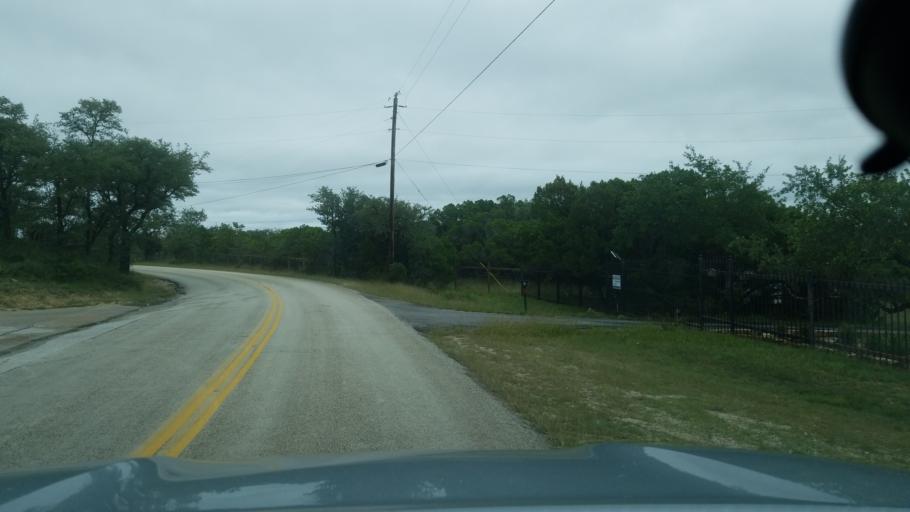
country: US
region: Texas
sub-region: Comal County
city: Bulverde
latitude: 29.7930
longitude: -98.4280
